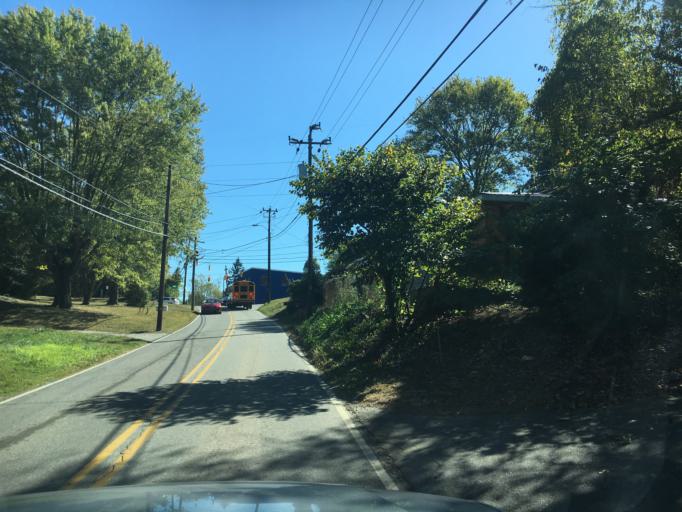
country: US
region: North Carolina
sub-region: Buncombe County
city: Woodfin
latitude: 35.6306
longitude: -82.5761
